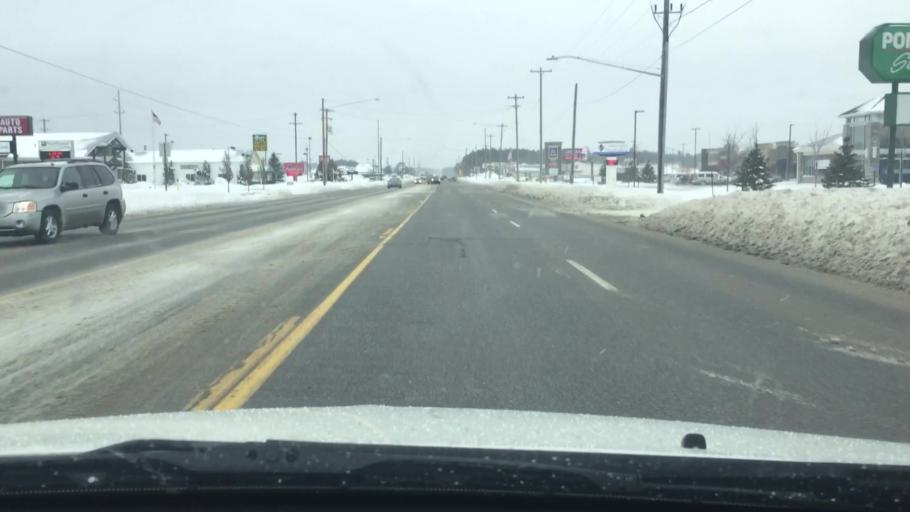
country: US
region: Michigan
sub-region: Otsego County
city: Gaylord
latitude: 45.0275
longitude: -84.6962
